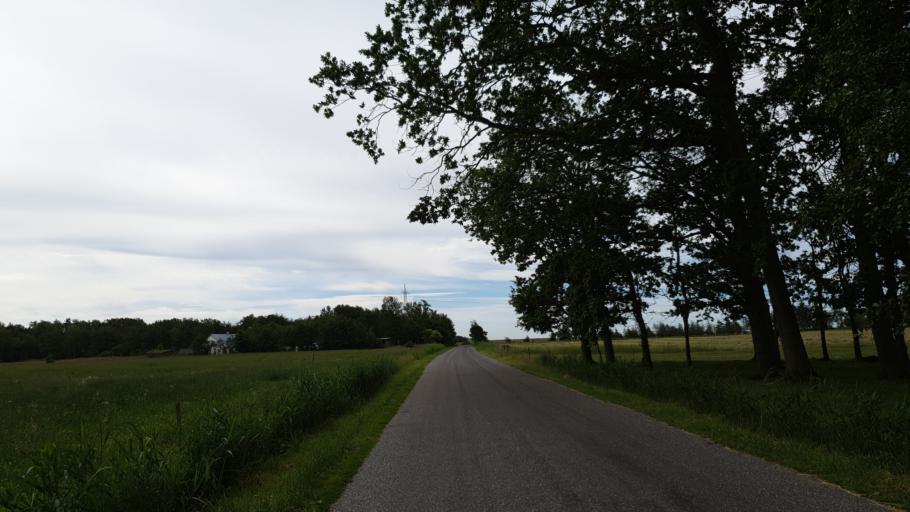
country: DK
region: North Denmark
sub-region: Laeso Kommune
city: Byrum
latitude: 57.2475
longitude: 10.9851
